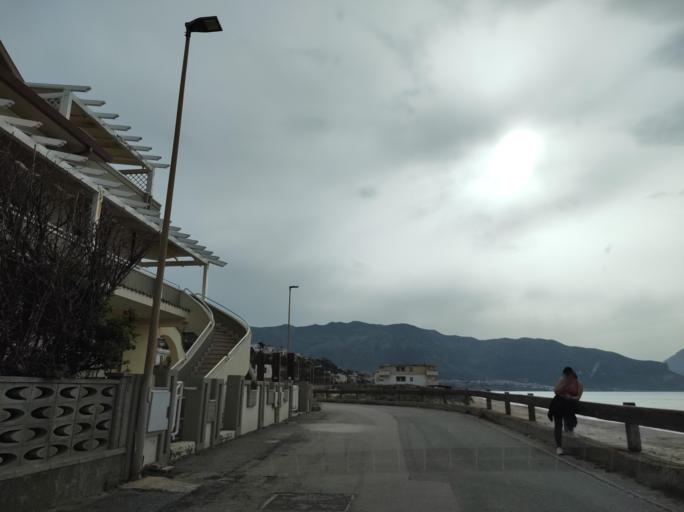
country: IT
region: Sicily
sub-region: Trapani
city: Alcamo
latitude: 38.0304
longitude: 12.9440
